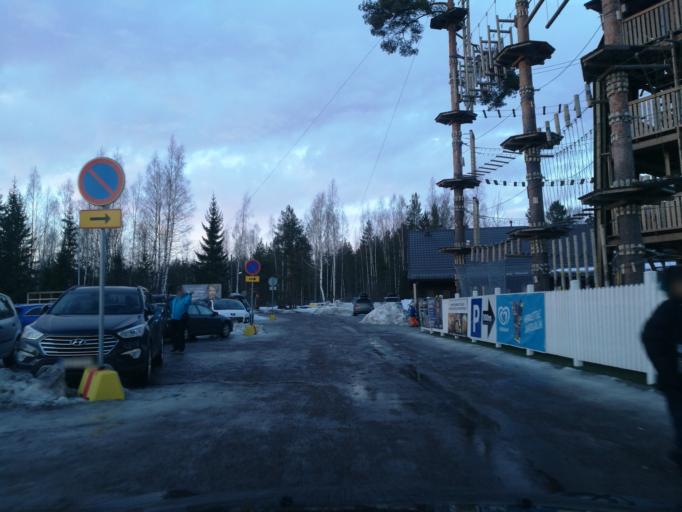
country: FI
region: Uusimaa
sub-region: Helsinki
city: Kerava
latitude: 60.3973
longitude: 25.1755
